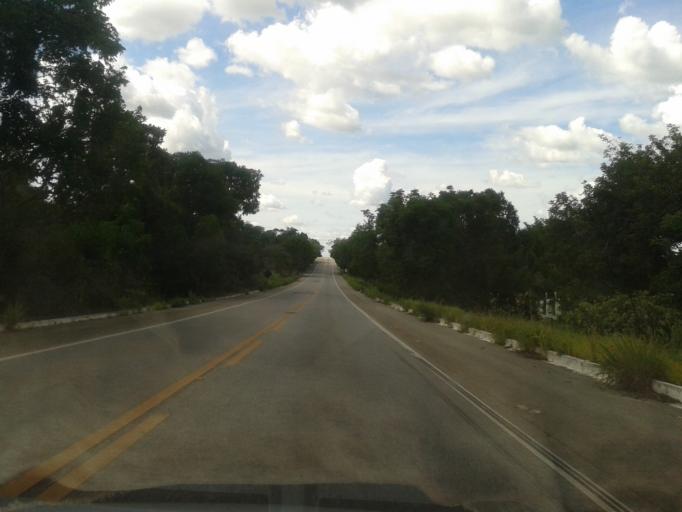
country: BR
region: Goias
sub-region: Itapuranga
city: Itapuranga
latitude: -15.5425
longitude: -50.2892
